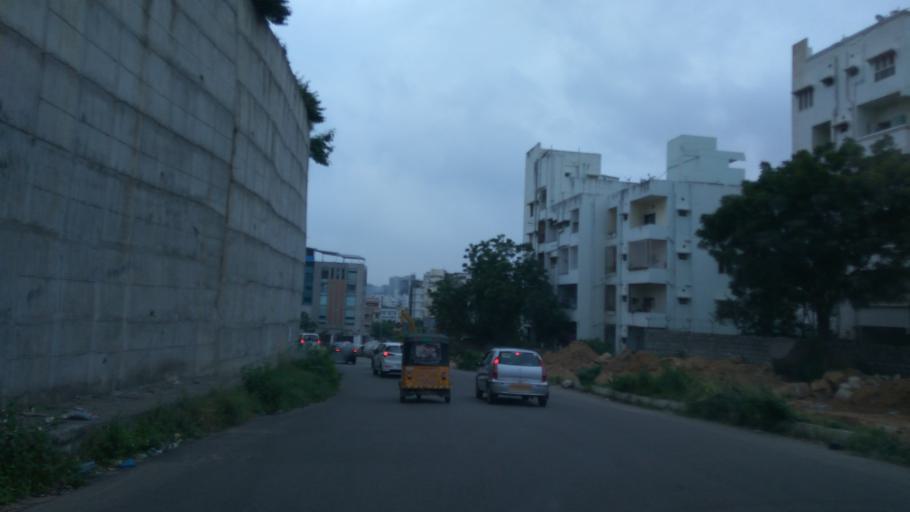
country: IN
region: Telangana
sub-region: Rangareddi
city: Kukatpalli
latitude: 17.4349
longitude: 78.3958
